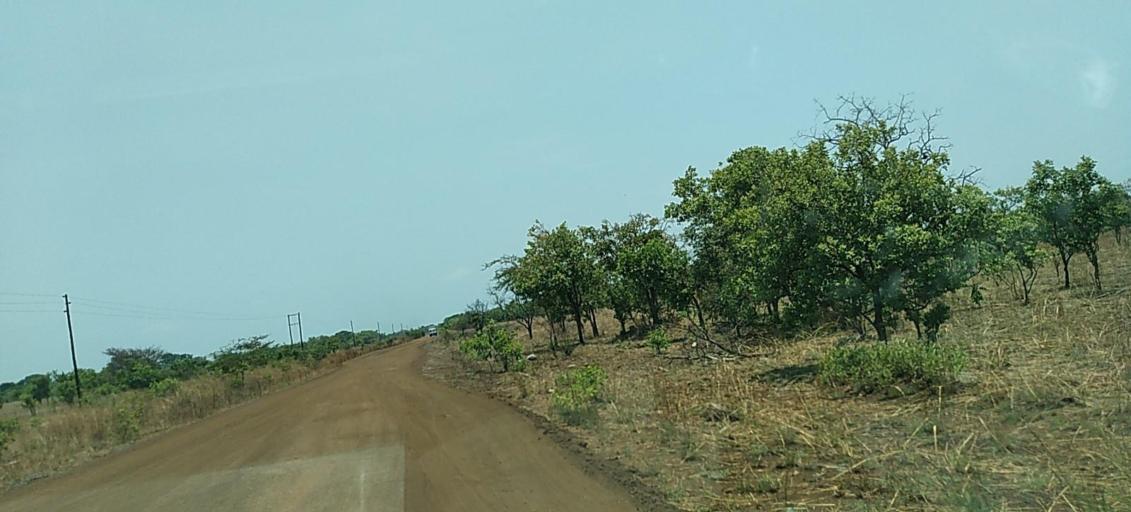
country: ZM
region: Copperbelt
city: Mpongwe
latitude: -13.7127
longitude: 27.8684
